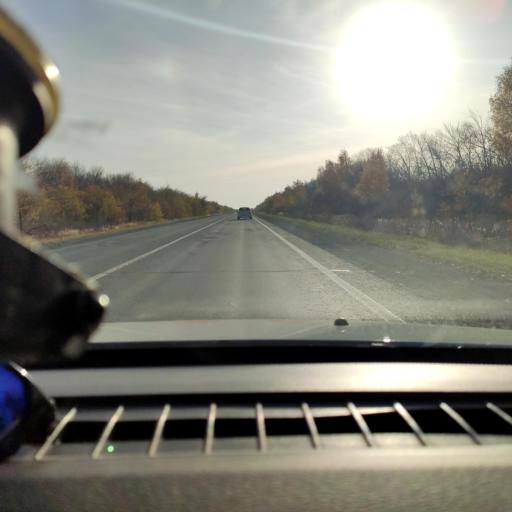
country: RU
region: Samara
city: Novokuybyshevsk
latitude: 52.9888
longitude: 49.8532
